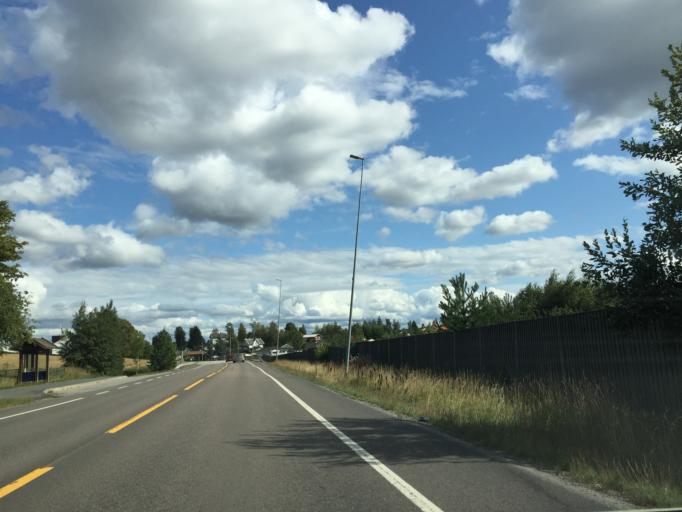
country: NO
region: Ostfold
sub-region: Spydeberg
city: Spydeberg
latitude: 59.6163
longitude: 11.0613
